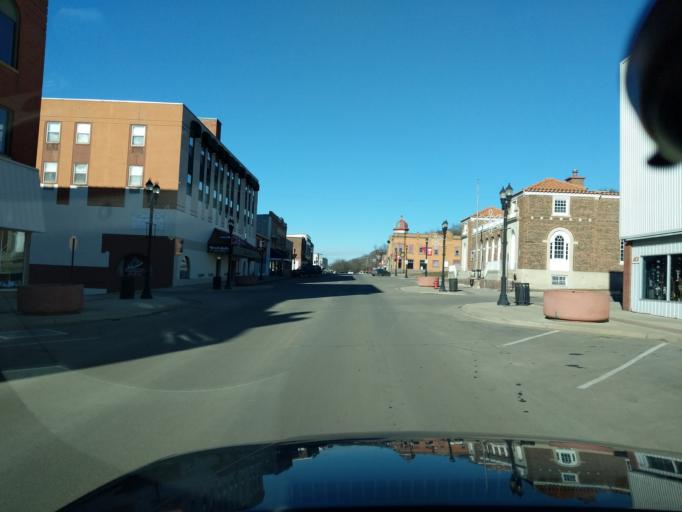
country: US
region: Minnesota
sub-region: Chippewa County
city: Montevideo
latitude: 44.9461
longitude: -95.7245
